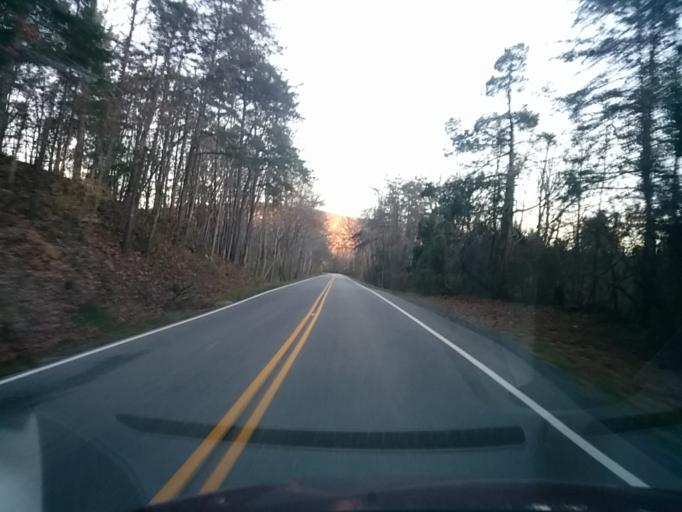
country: US
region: Virginia
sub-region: Rockbridge County
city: East Lexington
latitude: 37.9519
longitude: -79.4657
